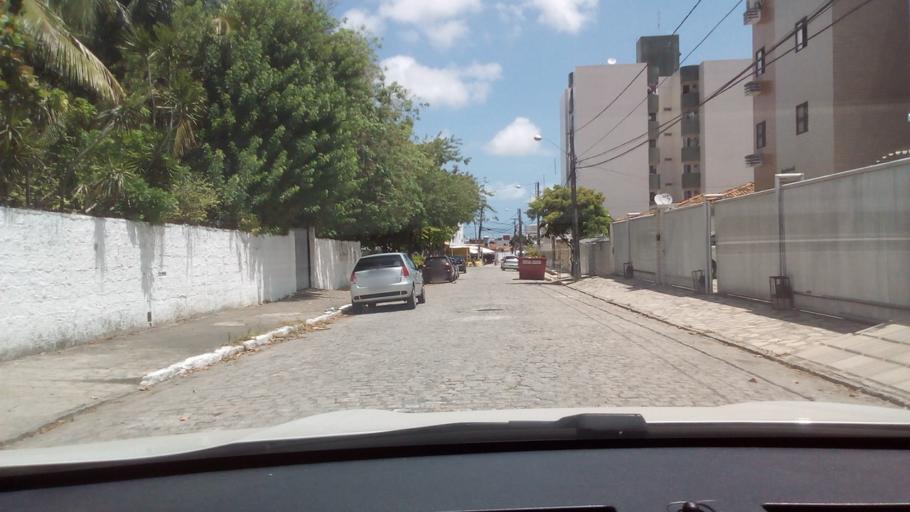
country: BR
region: Paraiba
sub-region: Joao Pessoa
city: Joao Pessoa
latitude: -7.1488
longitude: -34.8494
